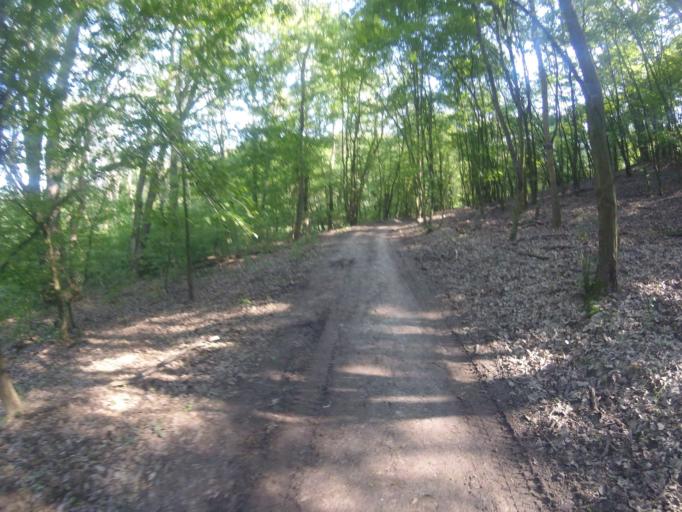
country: HU
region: Pest
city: Nagymaros
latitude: 47.8194
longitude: 18.9375
